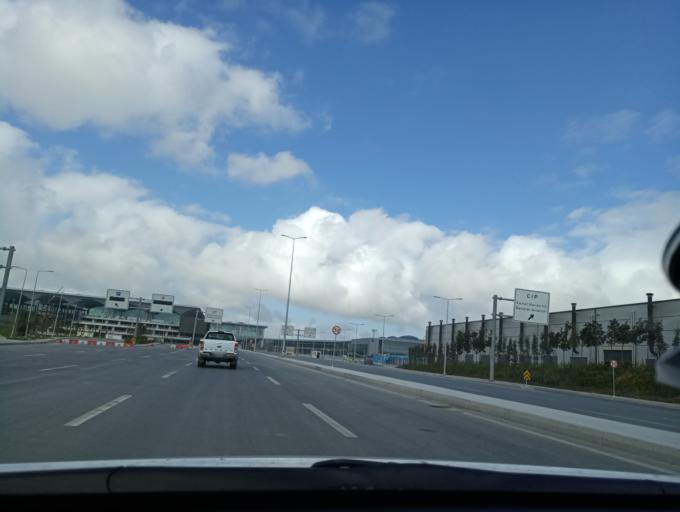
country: TR
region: Istanbul
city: Durusu
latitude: 41.2537
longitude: 28.7465
